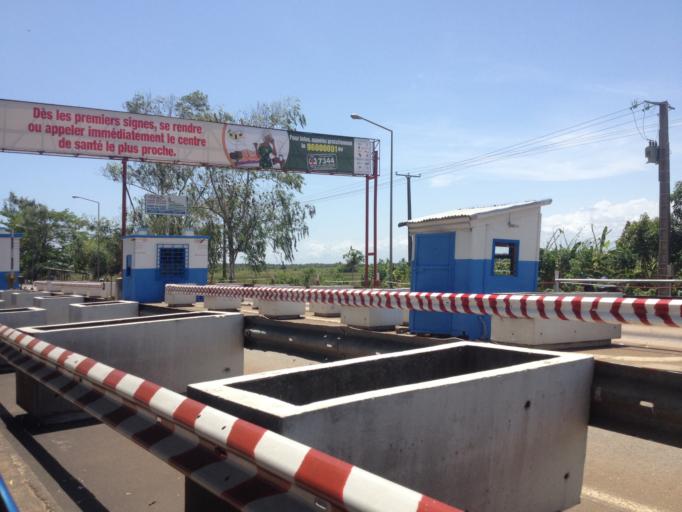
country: BJ
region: Mono
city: Grand-Popo
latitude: 6.2942
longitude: 1.8199
